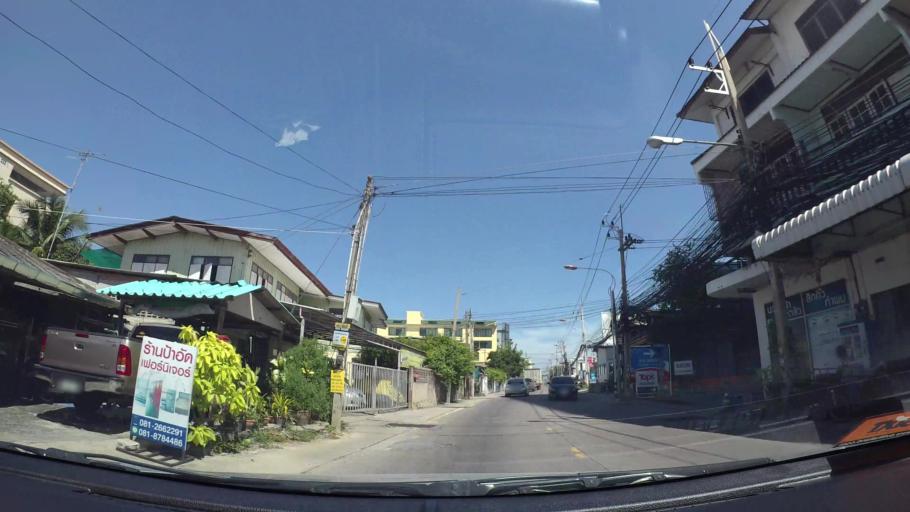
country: TH
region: Chon Buri
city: Si Racha
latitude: 13.1624
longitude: 100.9301
